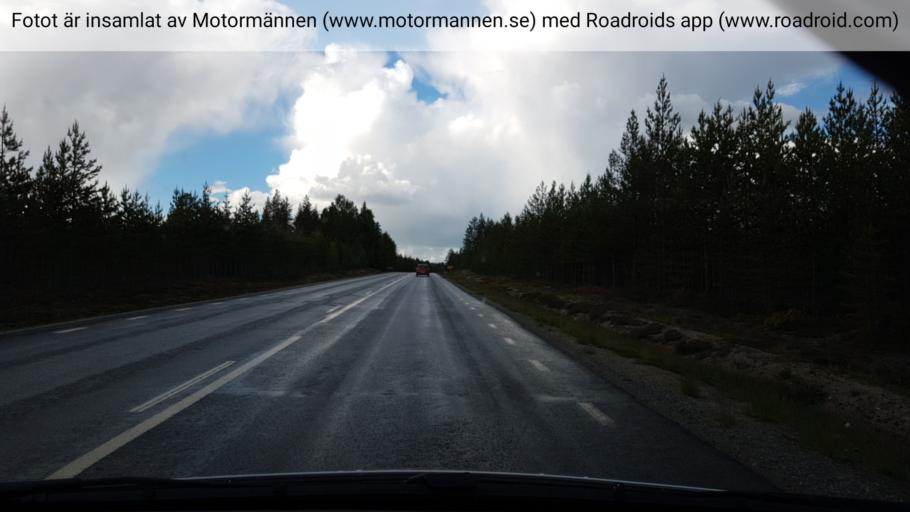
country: SE
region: Vaesterbotten
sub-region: Vannas Kommun
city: Vannasby
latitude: 64.0318
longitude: 20.0157
